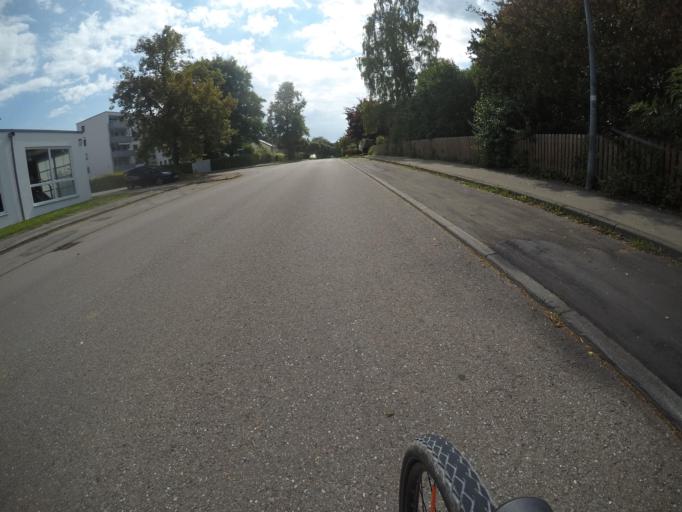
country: DE
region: Baden-Wuerttemberg
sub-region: Tuebingen Region
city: Munsingen
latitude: 48.4068
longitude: 9.4937
